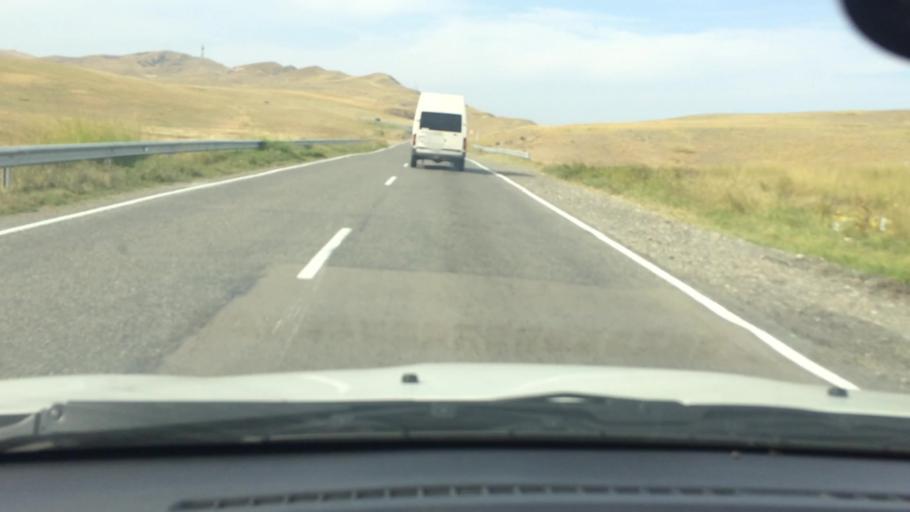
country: GE
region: Kvemo Kartli
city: Rust'avi
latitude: 41.5298
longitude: 44.9788
